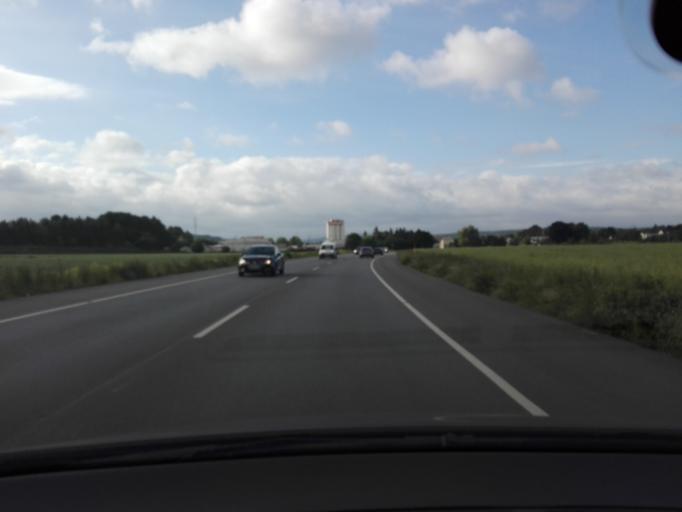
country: DE
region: North Rhine-Westphalia
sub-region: Regierungsbezirk Arnsberg
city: Frondenberg
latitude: 51.4639
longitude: 7.7748
